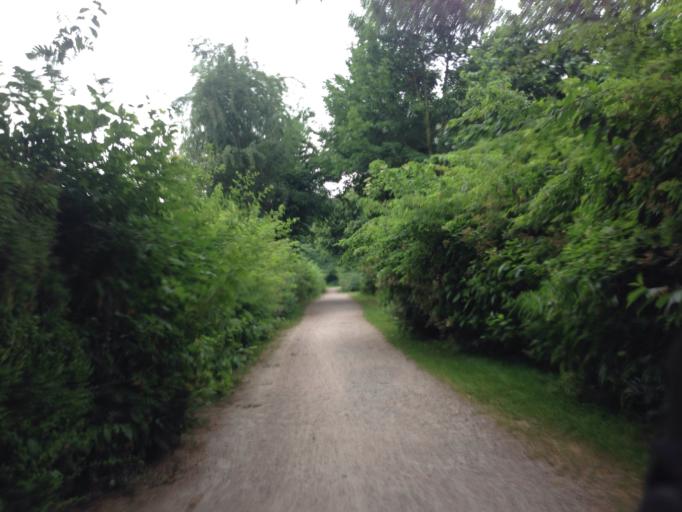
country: DE
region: Schleswig-Holstein
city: Barsbuettel
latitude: 53.5833
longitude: 10.1582
